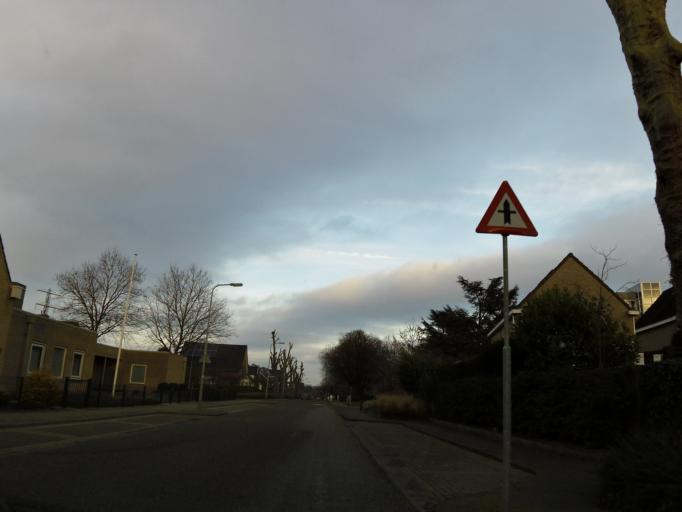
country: NL
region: Limburg
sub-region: Gemeente Heerlen
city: Mariarade
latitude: 50.9328
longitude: 5.9410
